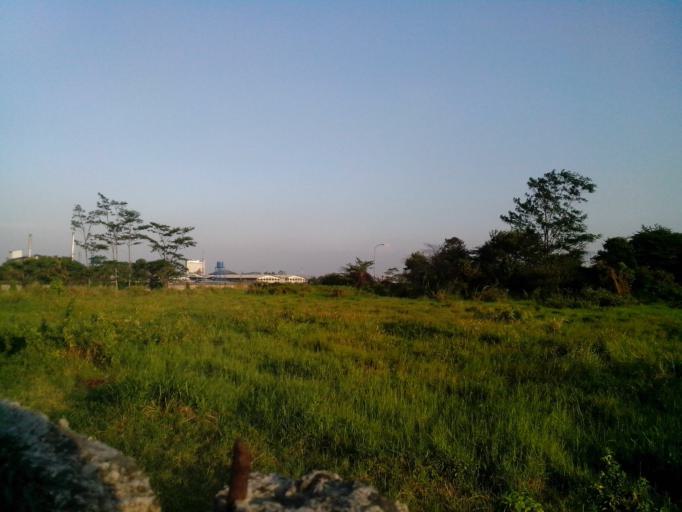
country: ID
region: West Java
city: Bandung
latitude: -6.9263
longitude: 107.6844
